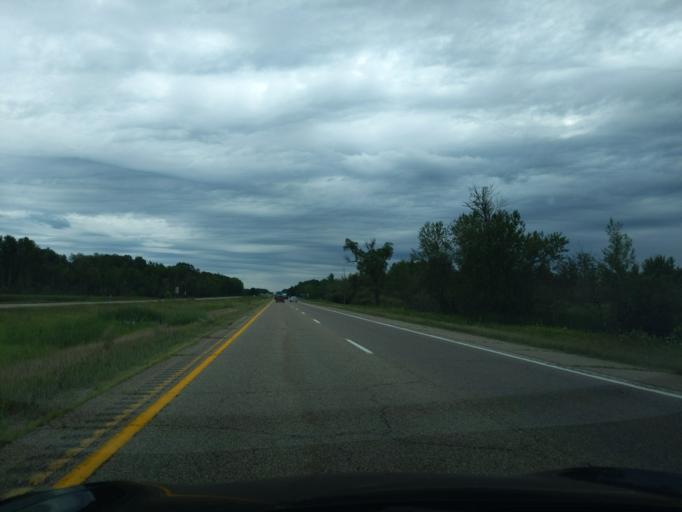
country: US
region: Michigan
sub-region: Roscommon County
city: Houghton Lake
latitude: 44.3484
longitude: -84.8077
